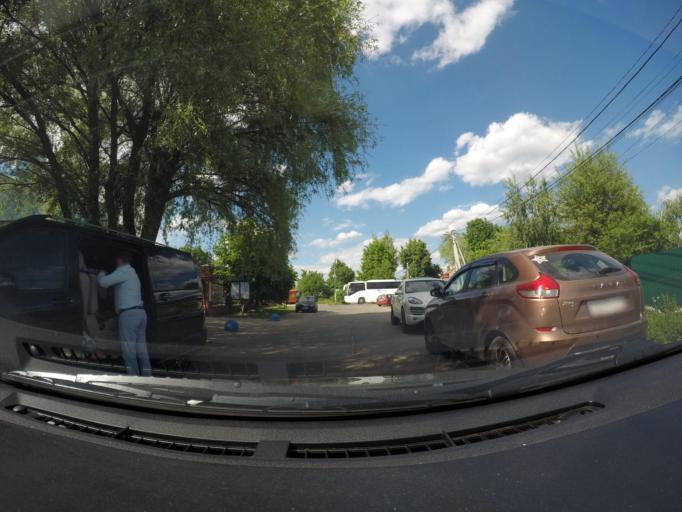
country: RU
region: Moskovskaya
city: Rechitsy
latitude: 55.5804
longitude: 38.5630
